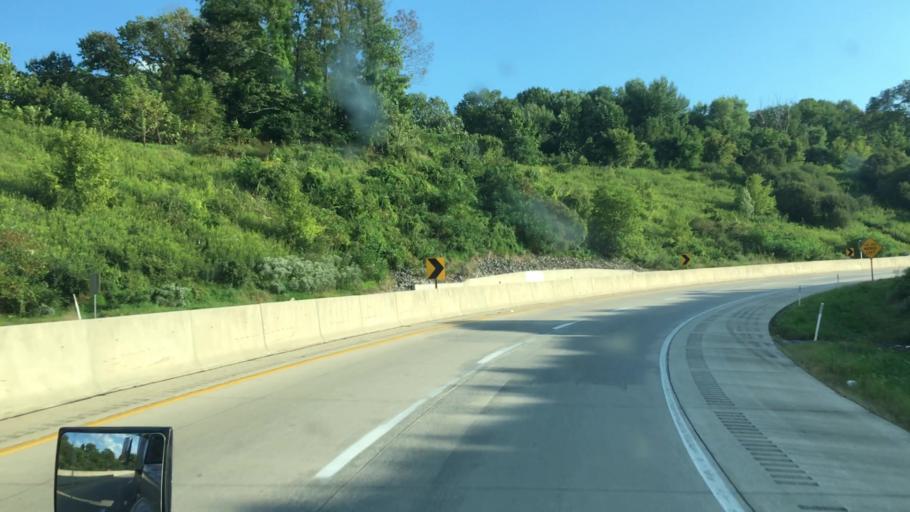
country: US
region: Pennsylvania
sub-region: Northampton County
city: Old Orchard
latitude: 40.6377
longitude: -75.2705
